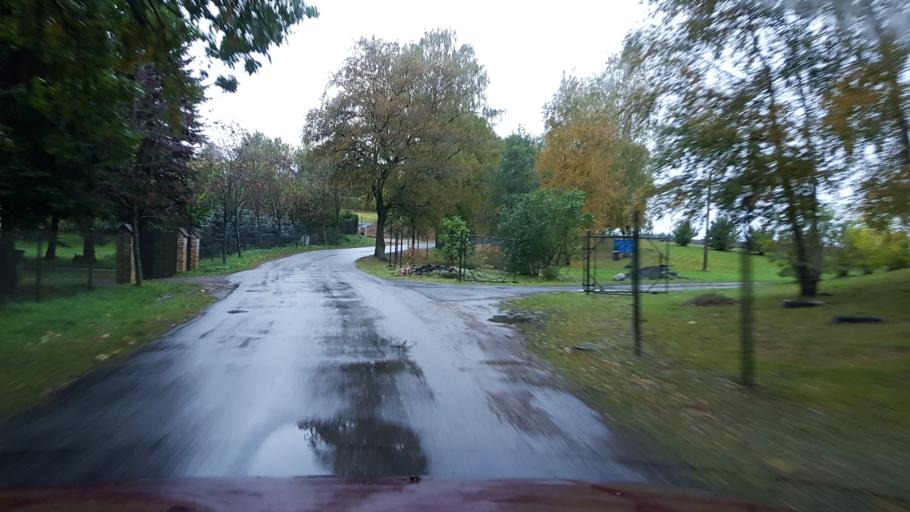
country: PL
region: West Pomeranian Voivodeship
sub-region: Koszalin
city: Koszalin
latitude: 54.1360
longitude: 16.1422
